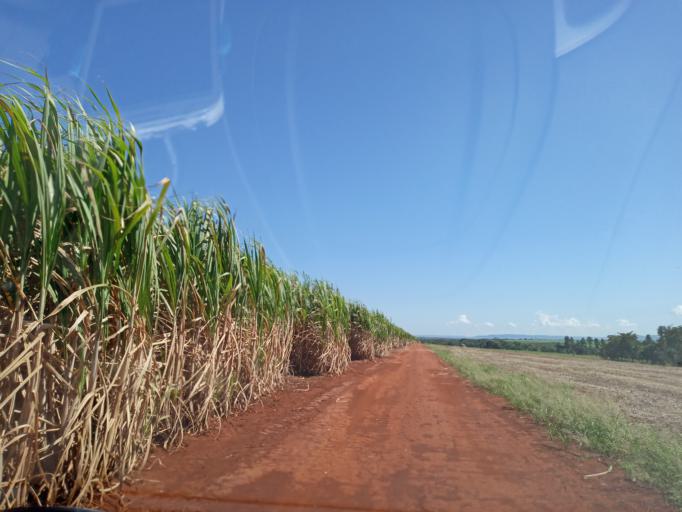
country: BR
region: Goias
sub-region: Itumbiara
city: Itumbiara
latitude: -18.4443
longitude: -49.1448
